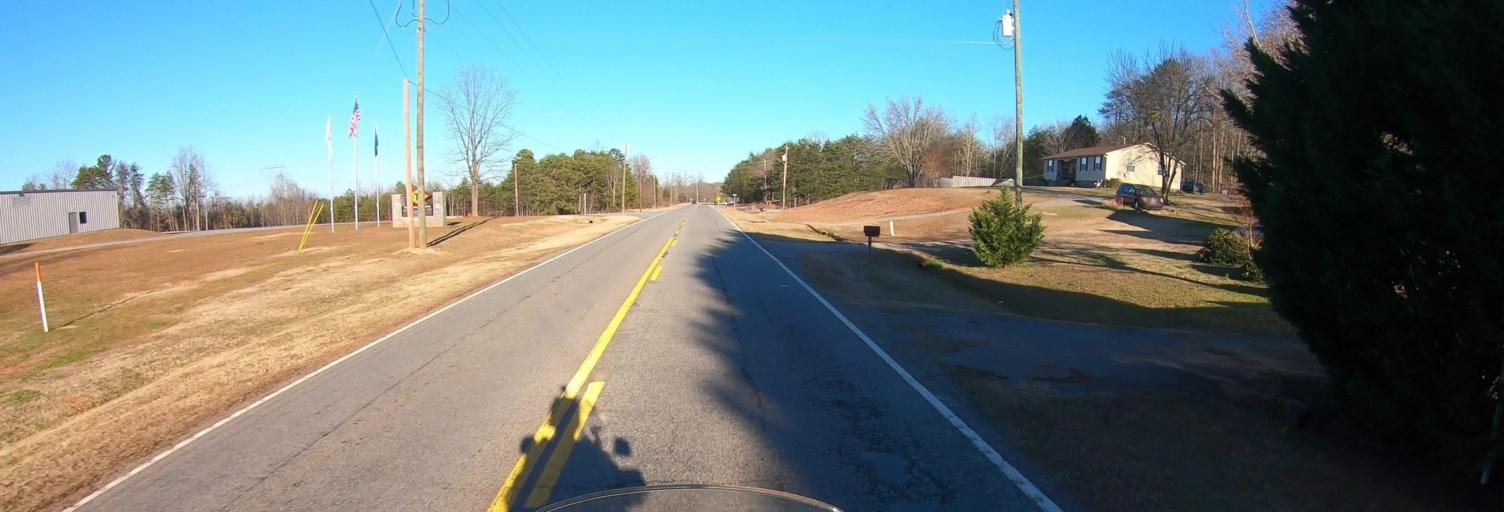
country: US
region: South Carolina
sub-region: Spartanburg County
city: Inman
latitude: 35.1413
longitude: -82.0863
